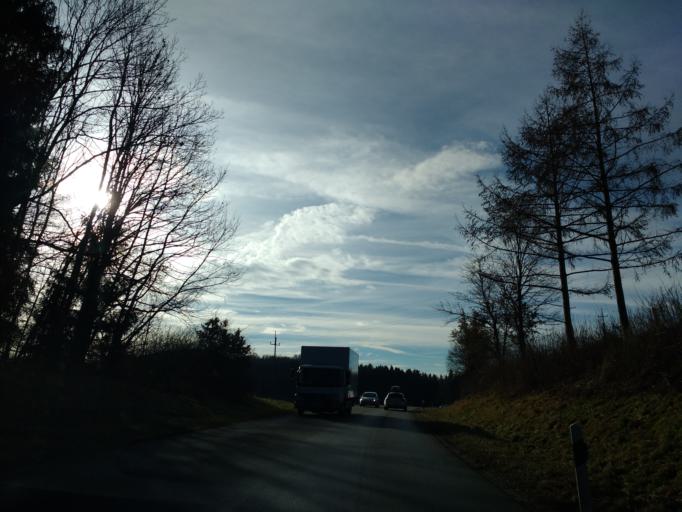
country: DE
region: Bavaria
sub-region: Swabia
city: Betzigau
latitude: 47.7221
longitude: 10.3729
